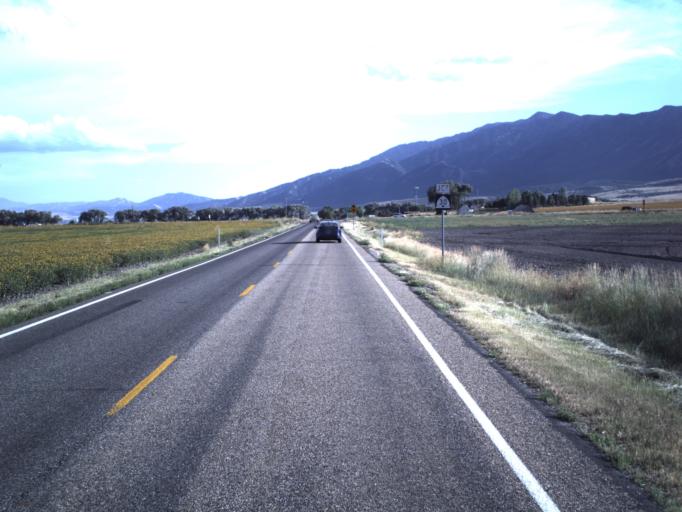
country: US
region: Utah
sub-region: Cache County
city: Mendon
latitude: 41.7541
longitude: -111.9795
